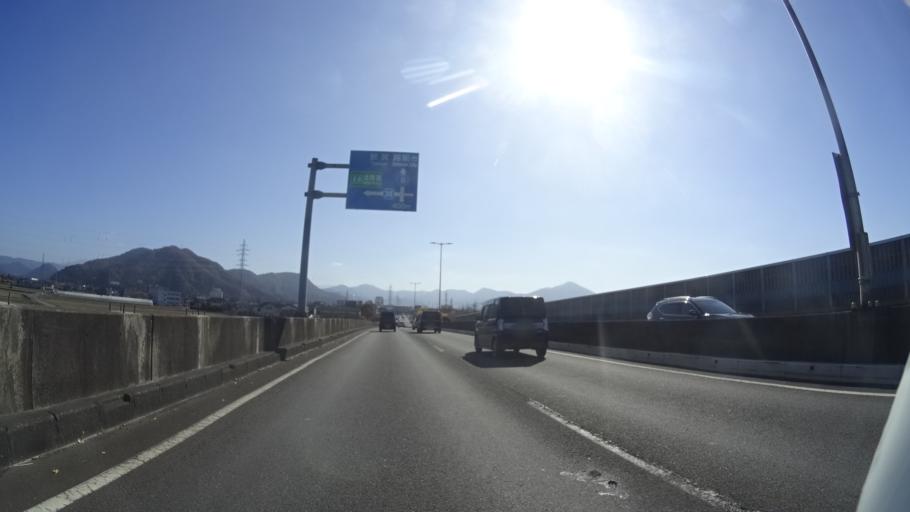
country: JP
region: Fukui
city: Sabae
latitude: 35.9528
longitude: 136.1909
